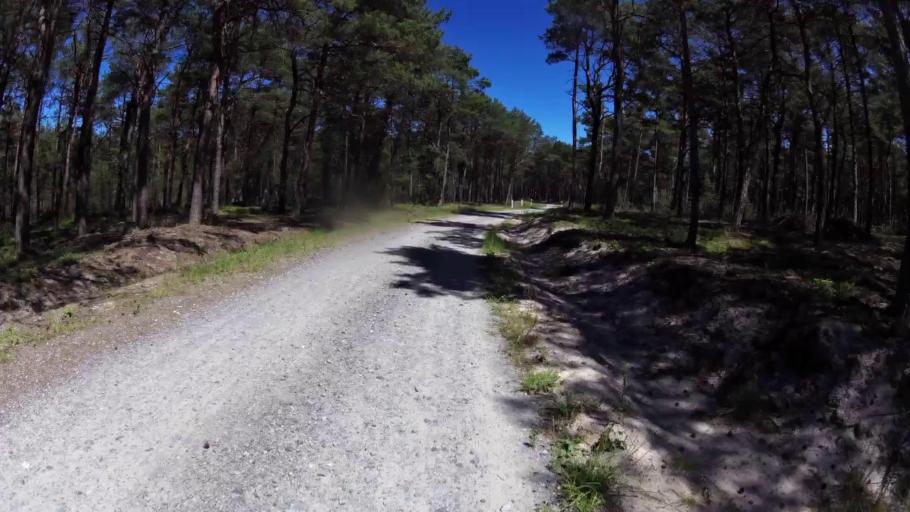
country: PL
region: West Pomeranian Voivodeship
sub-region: Powiat gryficki
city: Trzebiatow
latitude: 54.1201
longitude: 15.2084
